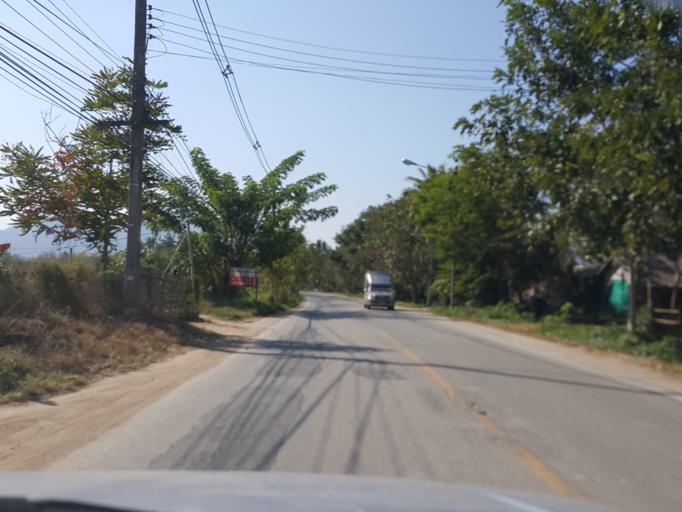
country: TH
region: Chiang Mai
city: Mae Wang
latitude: 18.6046
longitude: 98.7953
